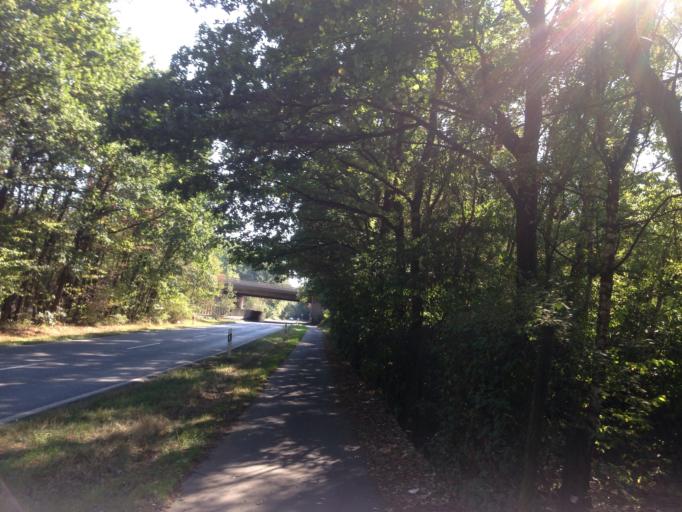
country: DE
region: Hesse
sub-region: Regierungsbezirk Giessen
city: Giessen
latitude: 50.5641
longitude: 8.6951
